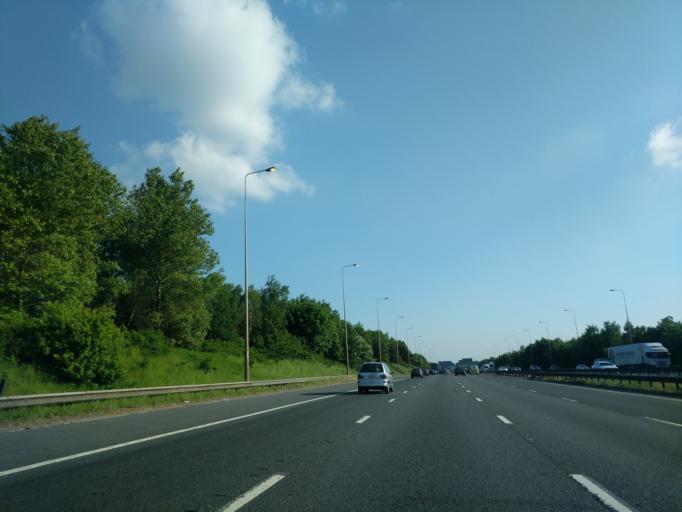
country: GB
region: England
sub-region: Warrington
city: Lymm
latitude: 53.3808
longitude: -2.5052
